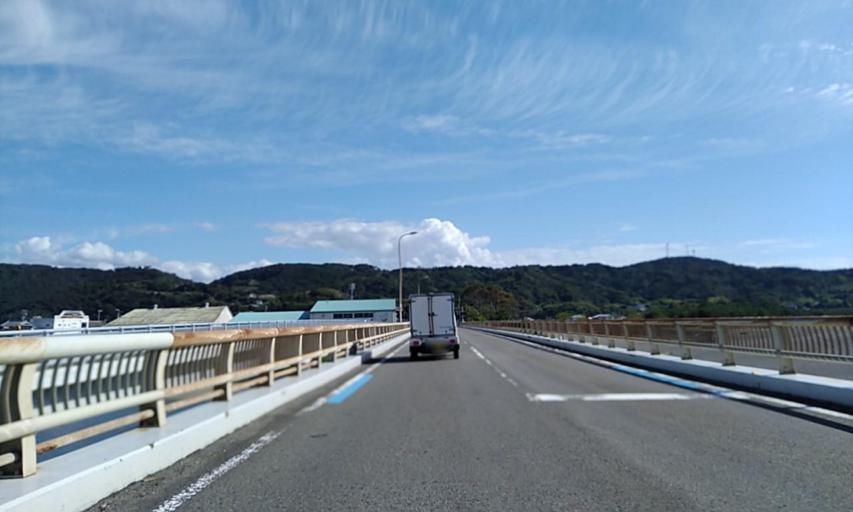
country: JP
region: Wakayama
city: Gobo
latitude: 33.7997
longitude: 135.2354
